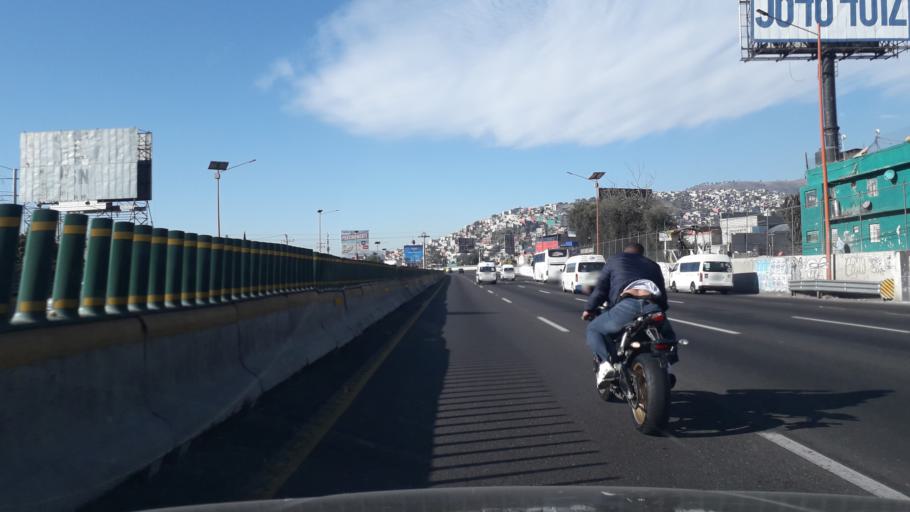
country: MX
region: Mexico
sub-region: Tlalnepantla de Baz
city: Puerto Escondido (Tepeolulco Puerto Escondido)
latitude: 19.5498
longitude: -99.0685
